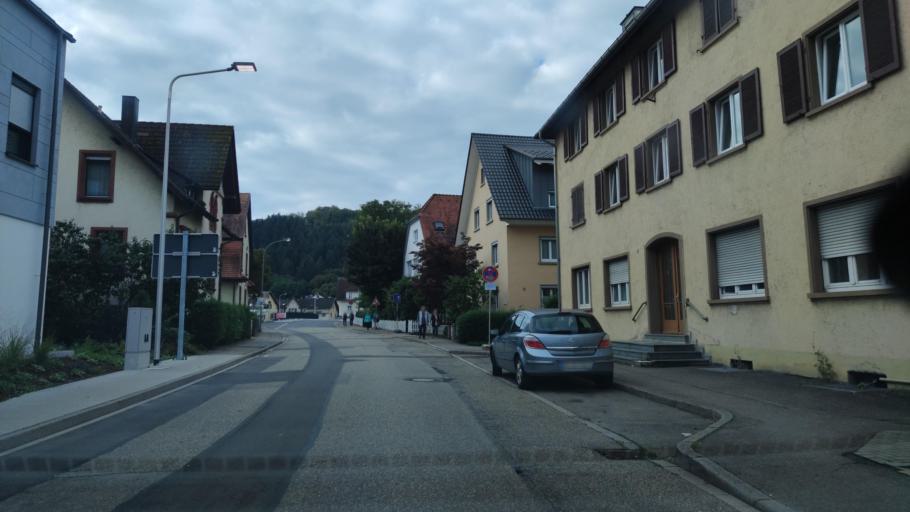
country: DE
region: Baden-Wuerttemberg
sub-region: Freiburg Region
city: Oberkirch
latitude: 48.5279
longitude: 8.0779
